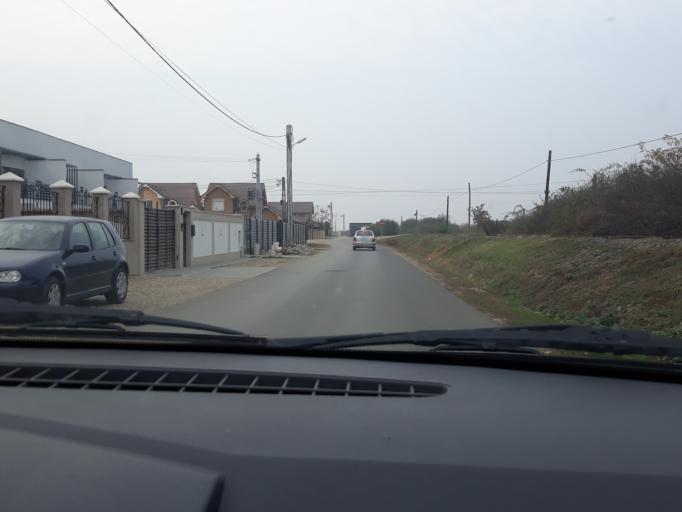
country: RO
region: Bihor
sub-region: Comuna Santandrei
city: Santandrei
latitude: 47.0635
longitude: 21.8523
